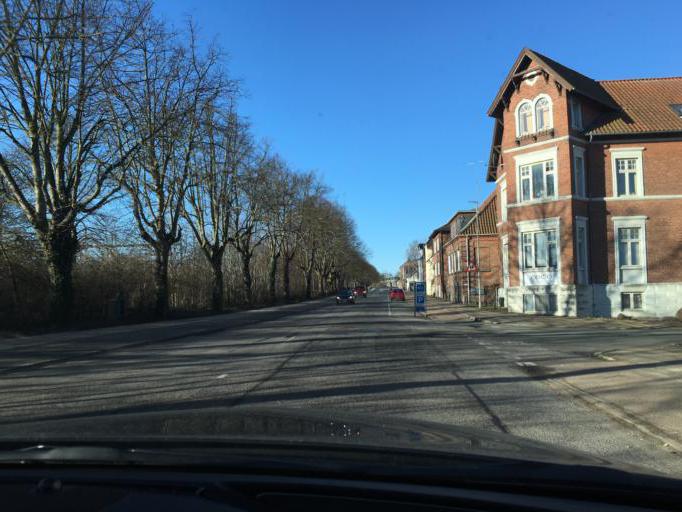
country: DK
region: South Denmark
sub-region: Kolding Kommune
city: Kolding
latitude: 55.4950
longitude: 9.4896
